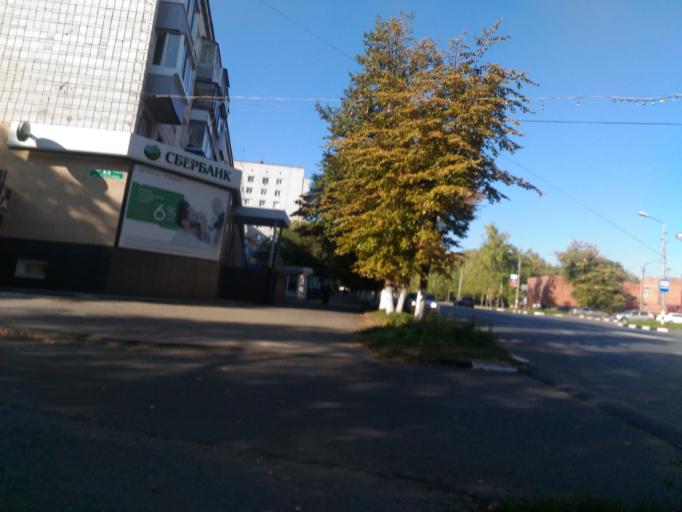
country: RU
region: Ulyanovsk
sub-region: Ulyanovskiy Rayon
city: Ulyanovsk
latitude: 54.3012
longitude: 48.3787
